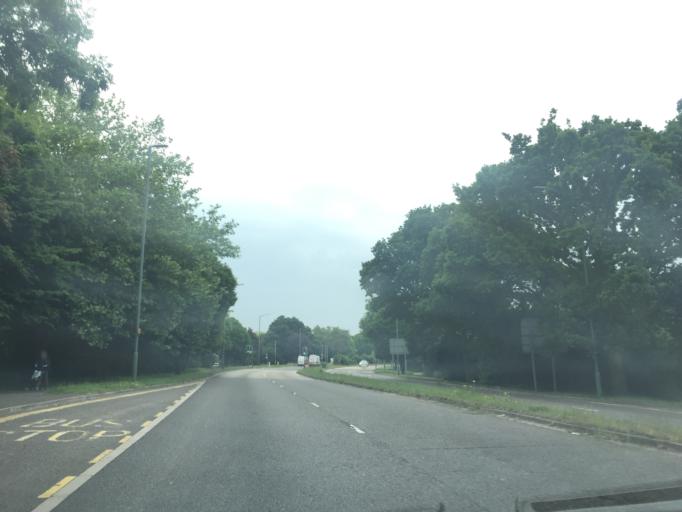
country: GB
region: England
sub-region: Dorset
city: Ferndown
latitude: 50.7690
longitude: -1.9196
